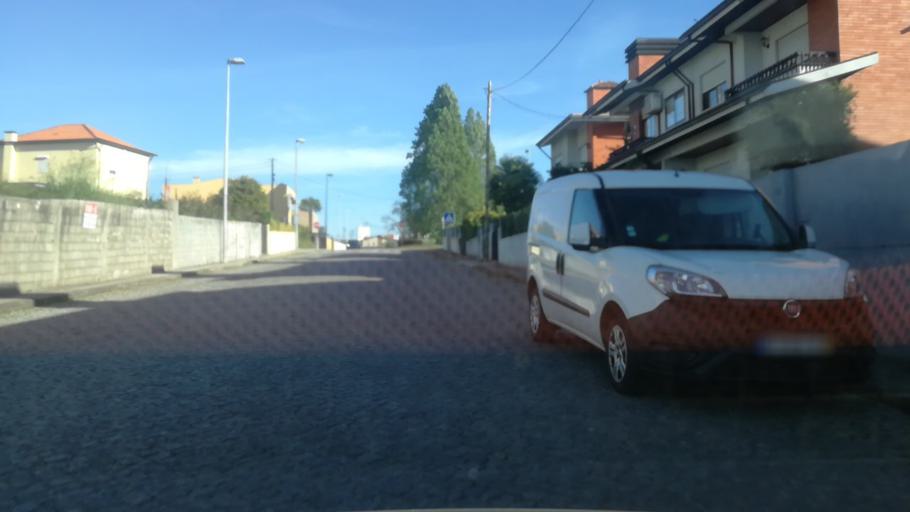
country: PT
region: Porto
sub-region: Maia
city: Gemunde
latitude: 41.2517
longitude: -8.6676
